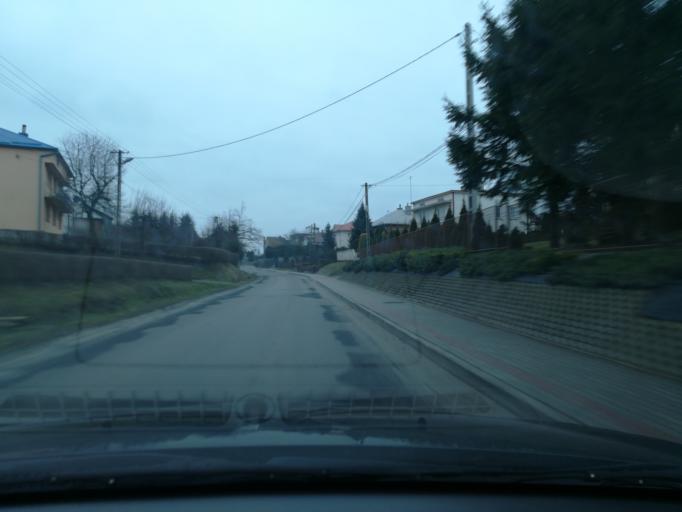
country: PL
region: Subcarpathian Voivodeship
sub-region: Powiat lancucki
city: Kosina
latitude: 50.0807
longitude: 22.3257
